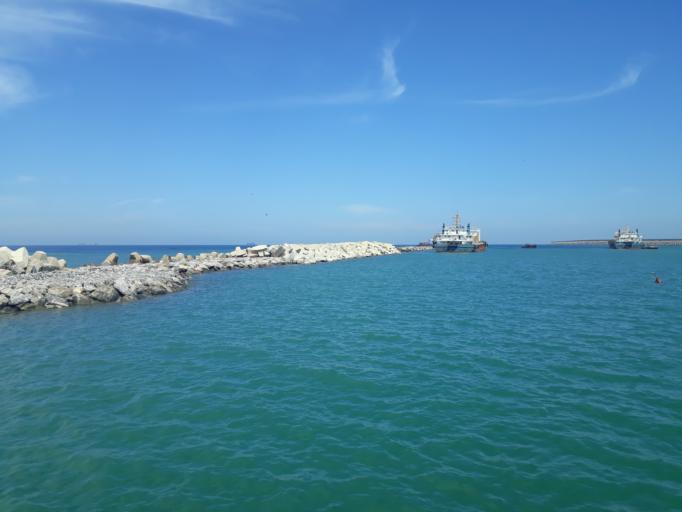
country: LK
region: Western
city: Colombo
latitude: 6.9311
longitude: 79.8210
